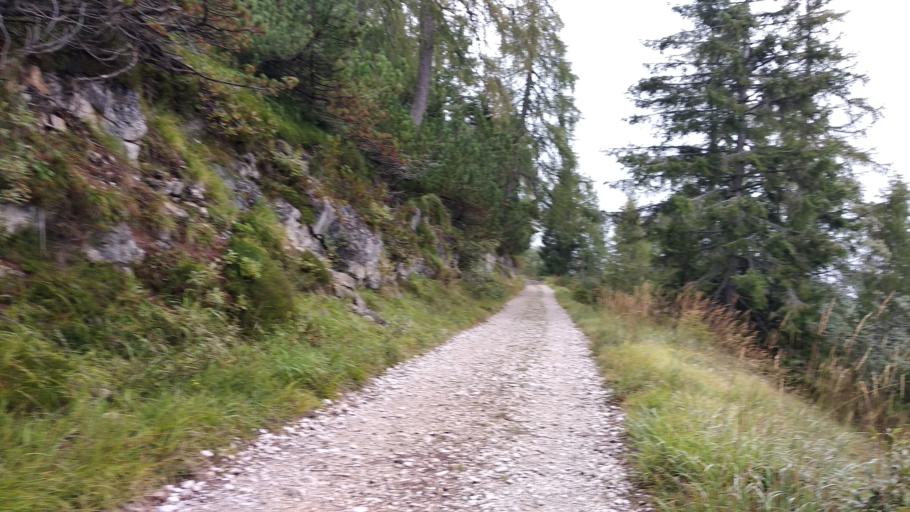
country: IT
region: Trentino-Alto Adige
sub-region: Provincia di Trento
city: Borgo
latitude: 45.9686
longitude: 11.4366
